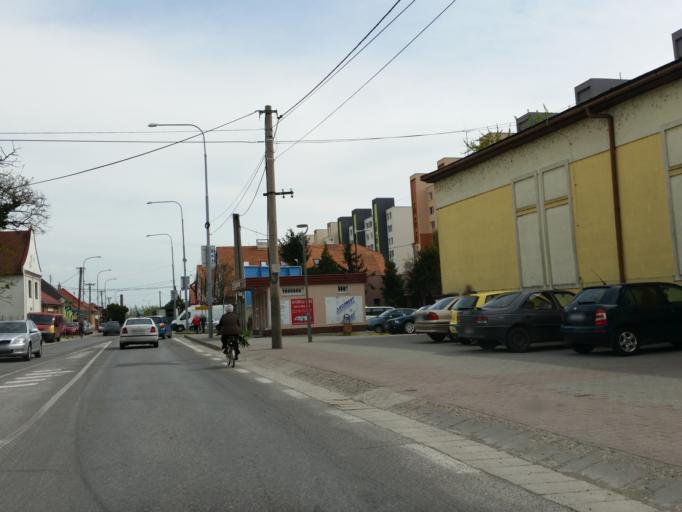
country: SK
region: Trnavsky
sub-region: Okres Dunajska Streda
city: Velky Meder
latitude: 47.8557
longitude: 17.7728
